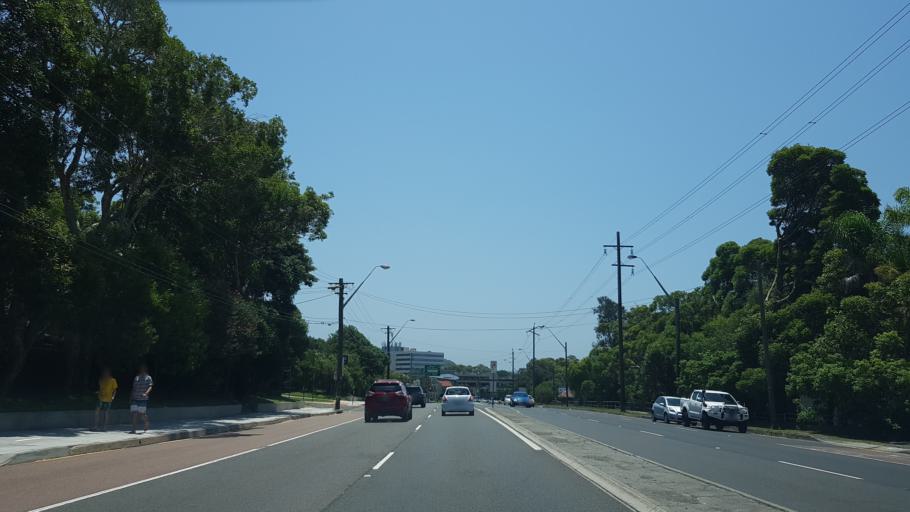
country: AU
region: New South Wales
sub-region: Pittwater
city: Warriewood
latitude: -33.6823
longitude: 151.3033
